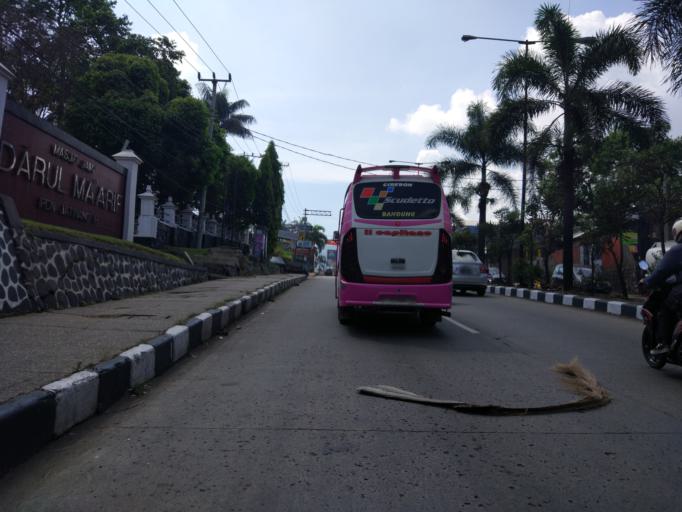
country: ID
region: West Java
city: Cileunyi
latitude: -6.9355
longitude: 107.7655
